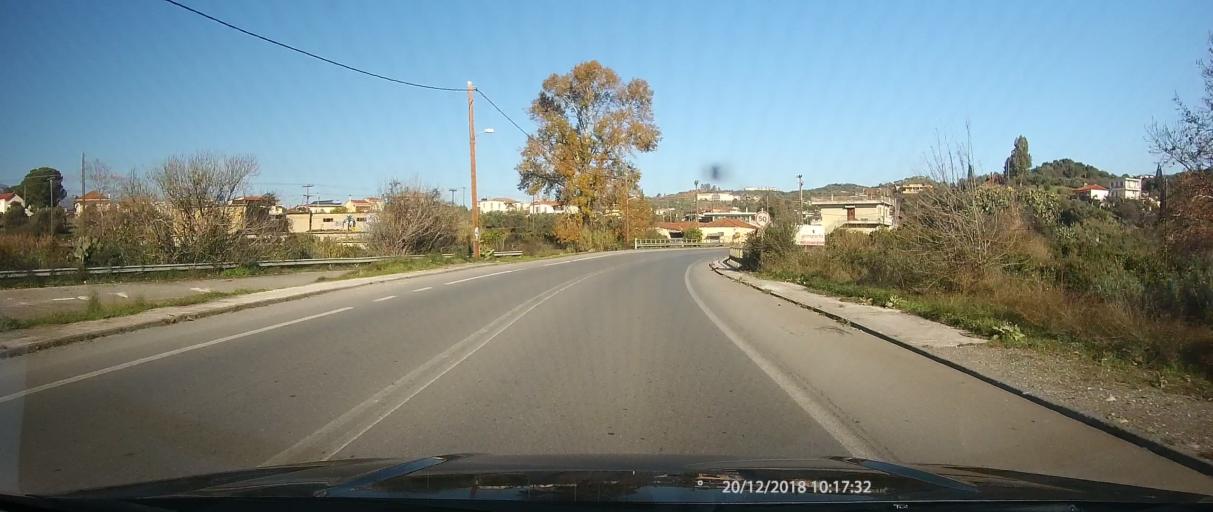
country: GR
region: Peloponnese
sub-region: Nomos Lakonias
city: Sparti
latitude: 37.1079
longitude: 22.4338
